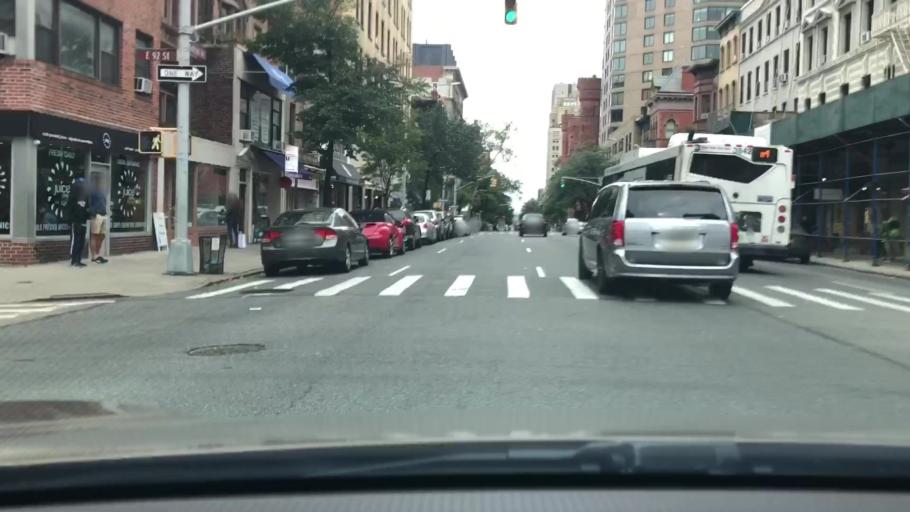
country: US
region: New York
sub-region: New York County
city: Manhattan
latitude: 40.7849
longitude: -73.9560
